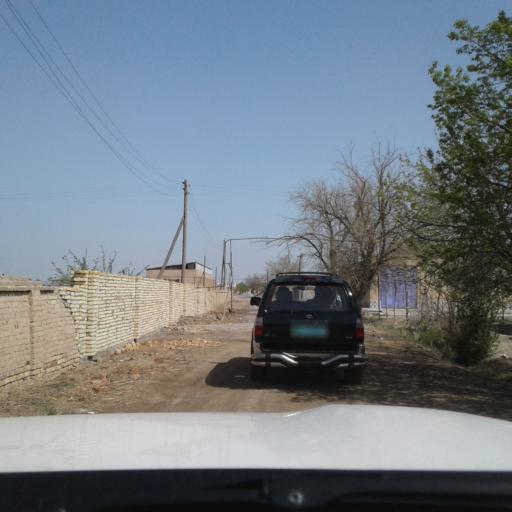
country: TM
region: Lebap
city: Turkmenabat
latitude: 38.9592
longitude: 63.6461
